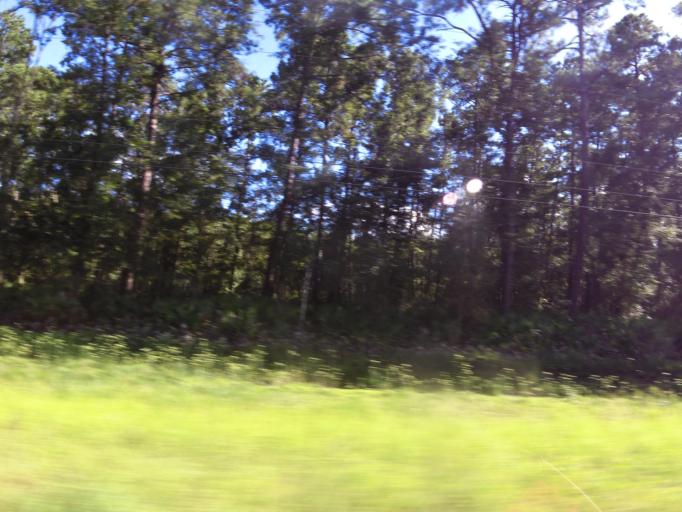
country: US
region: Georgia
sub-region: Glynn County
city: Brunswick
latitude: 31.1062
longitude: -81.6410
